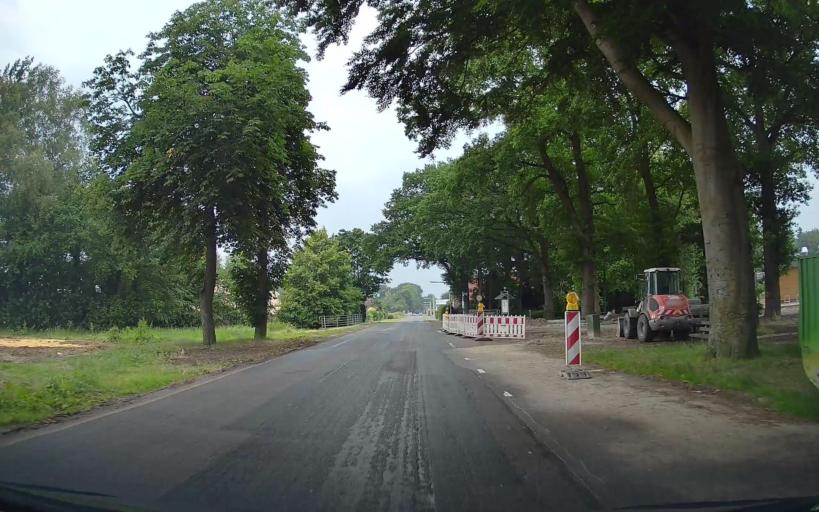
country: DE
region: Lower Saxony
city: Friesoythe
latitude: 53.0130
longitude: 7.8609
